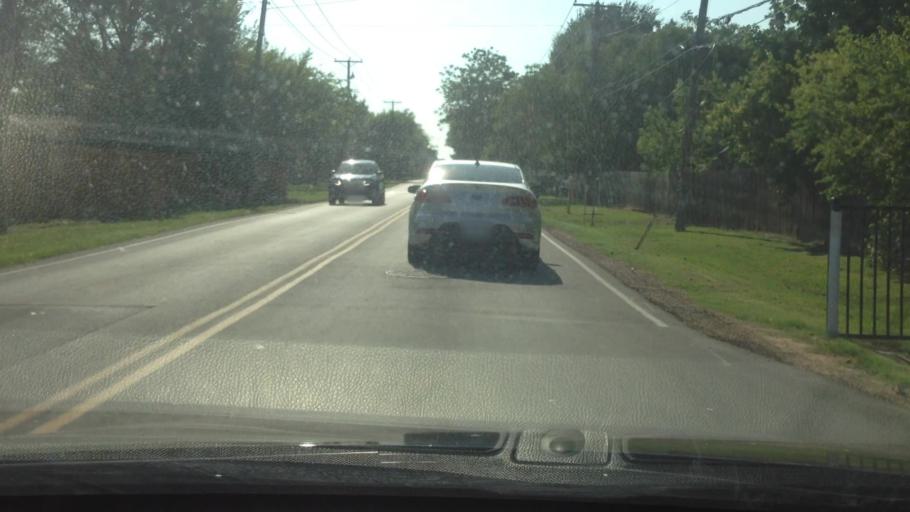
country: US
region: Texas
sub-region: Tarrant County
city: Watauga
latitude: 32.8677
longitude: -97.2403
